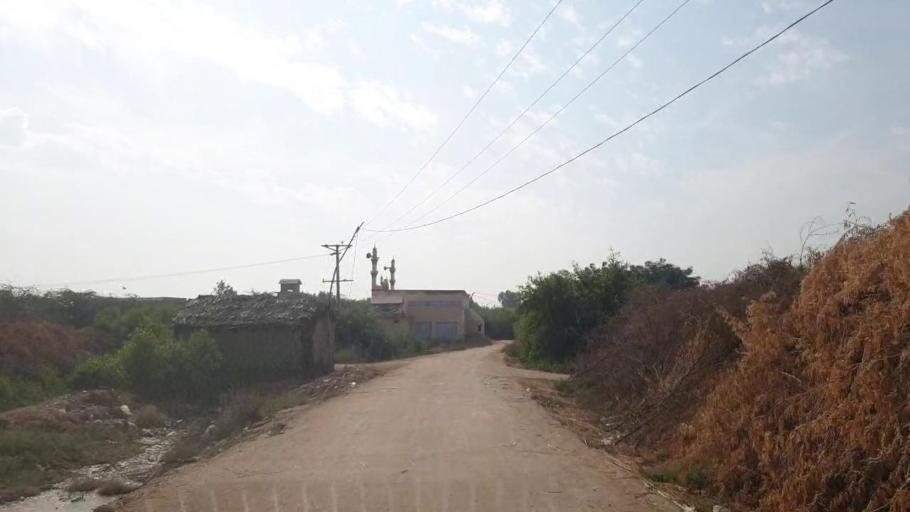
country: PK
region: Sindh
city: Tando Bago
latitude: 24.8843
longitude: 69.0035
